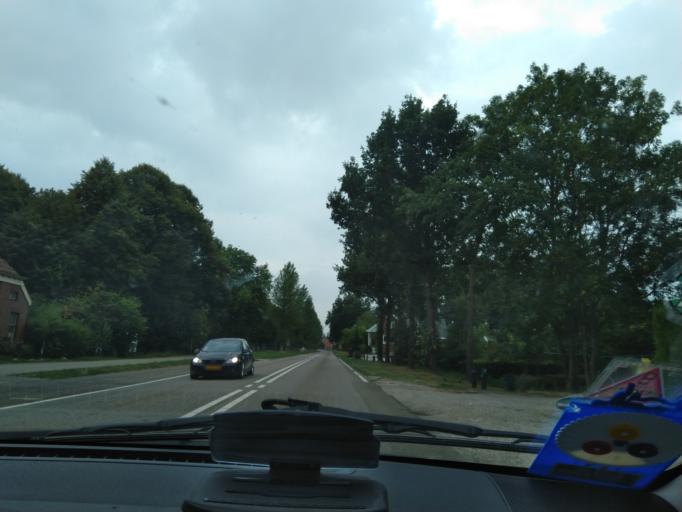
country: NL
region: Groningen
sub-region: Gemeente  Oldambt
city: Winschoten
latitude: 53.1118
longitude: 7.0878
